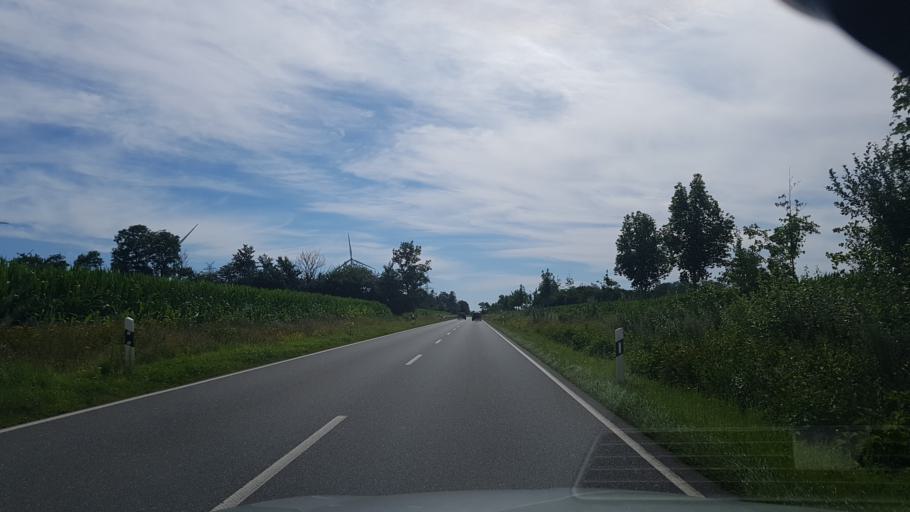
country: DE
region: Schleswig-Holstein
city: Boxlund
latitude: 54.8541
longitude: 9.1817
